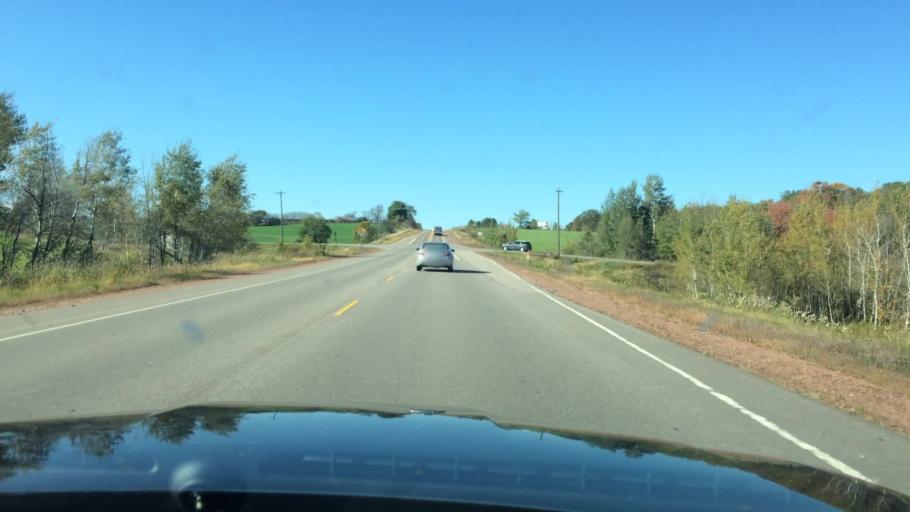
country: US
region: Wisconsin
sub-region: Marathon County
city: Wausau
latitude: 45.0015
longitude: -89.6681
